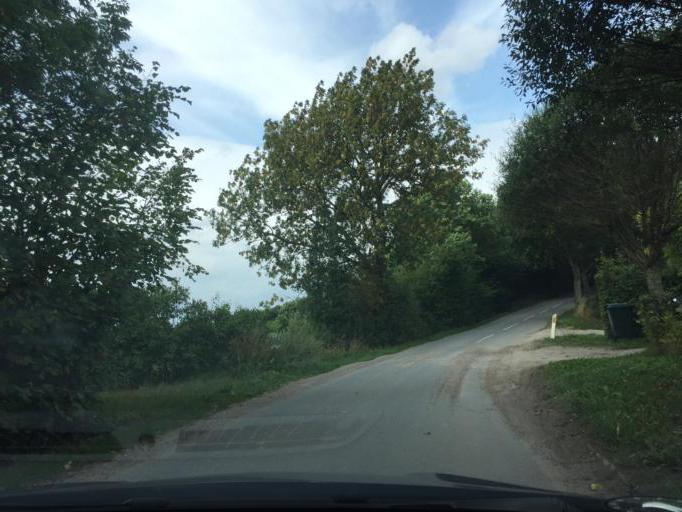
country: DK
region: South Denmark
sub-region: Assens Kommune
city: Tommerup Stationsby
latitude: 55.3775
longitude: 10.1726
